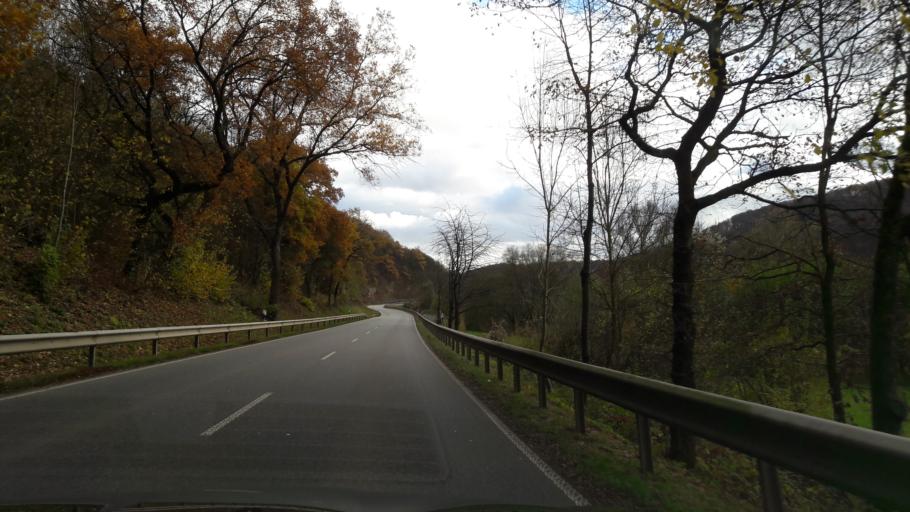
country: DE
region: Rheinland-Pfalz
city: Menningen
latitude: 49.8211
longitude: 6.4774
